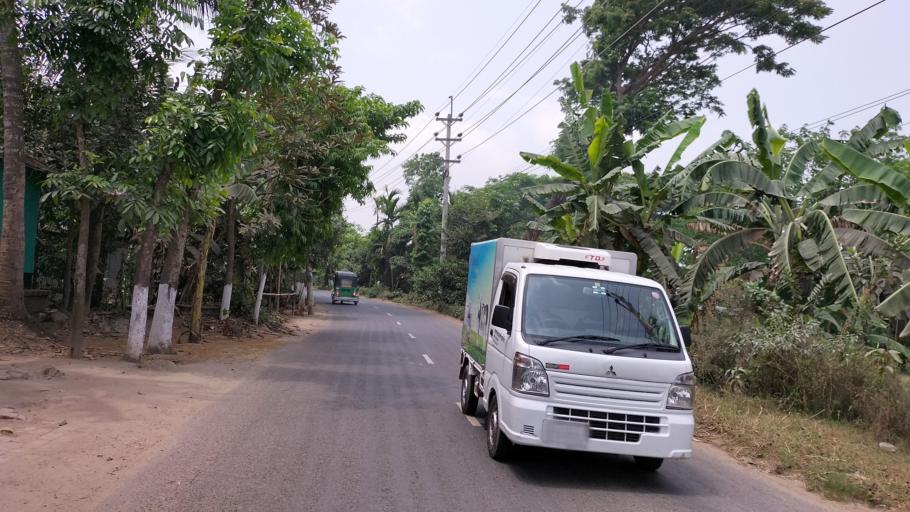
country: BD
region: Dhaka
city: Azimpur
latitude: 23.7312
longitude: 90.2993
